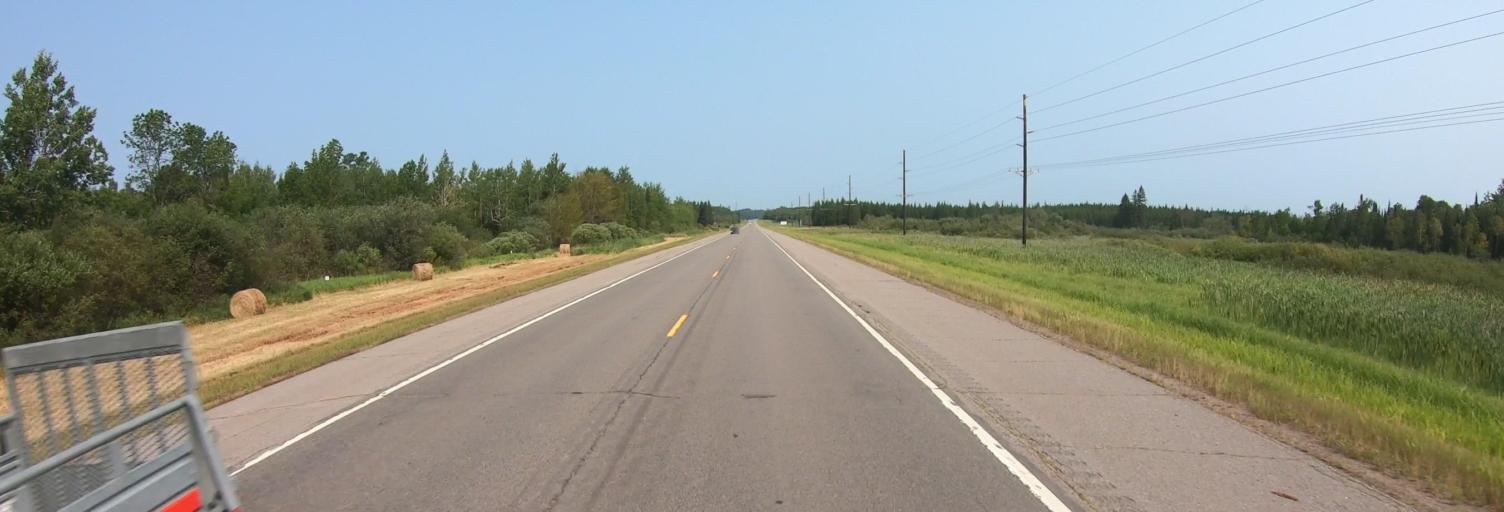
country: US
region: Minnesota
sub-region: Saint Louis County
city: Chisholm
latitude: 47.9405
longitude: -92.8281
